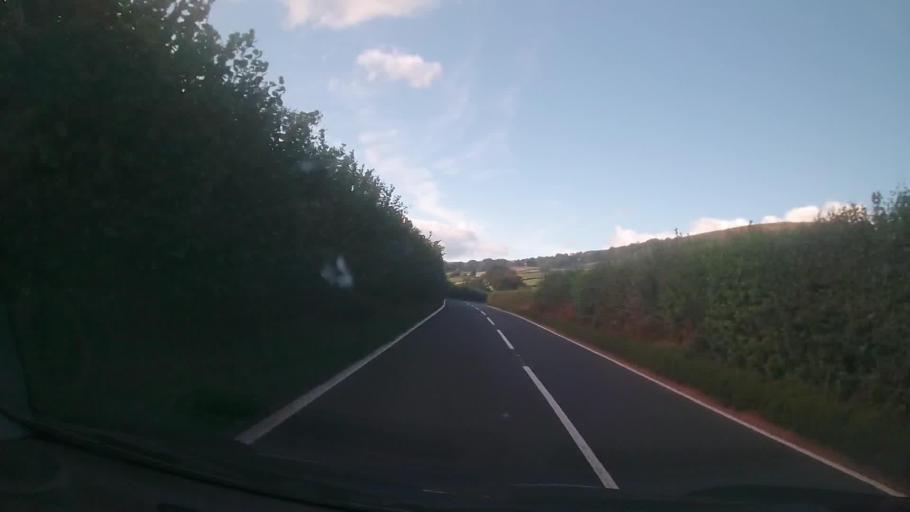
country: GB
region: Wales
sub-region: Blaenau Gwent
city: Brynmawr
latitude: 51.8758
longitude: -3.1730
